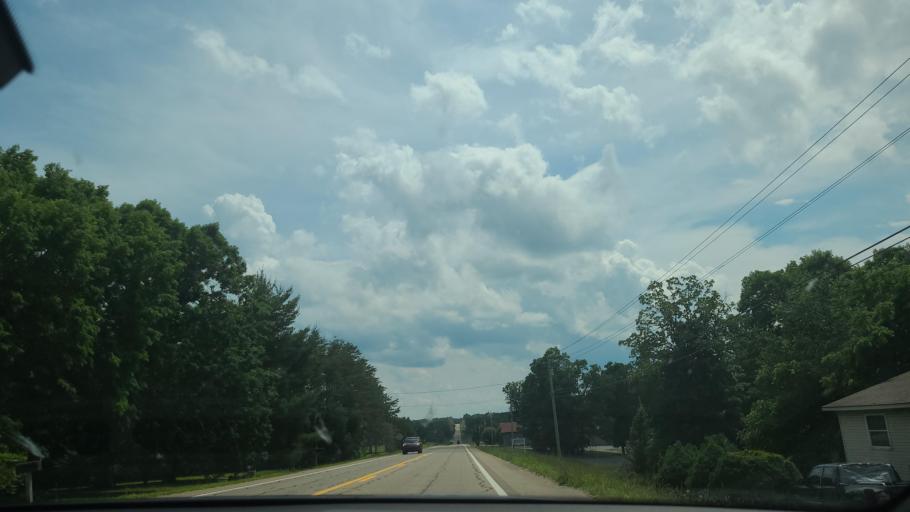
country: US
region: Tennessee
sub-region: Cumberland County
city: Lake Tansi
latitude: 35.8585
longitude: -85.0093
